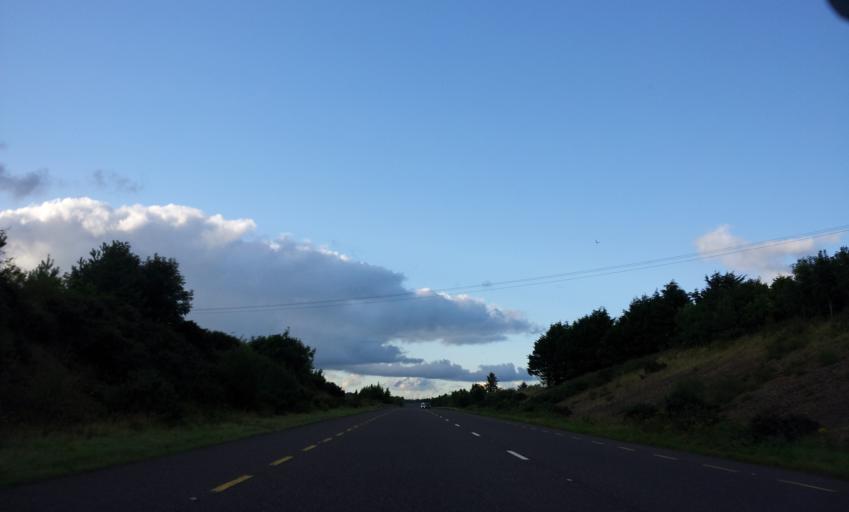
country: IE
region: Munster
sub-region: County Limerick
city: Abbeyfeale
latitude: 52.3211
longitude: -9.3594
